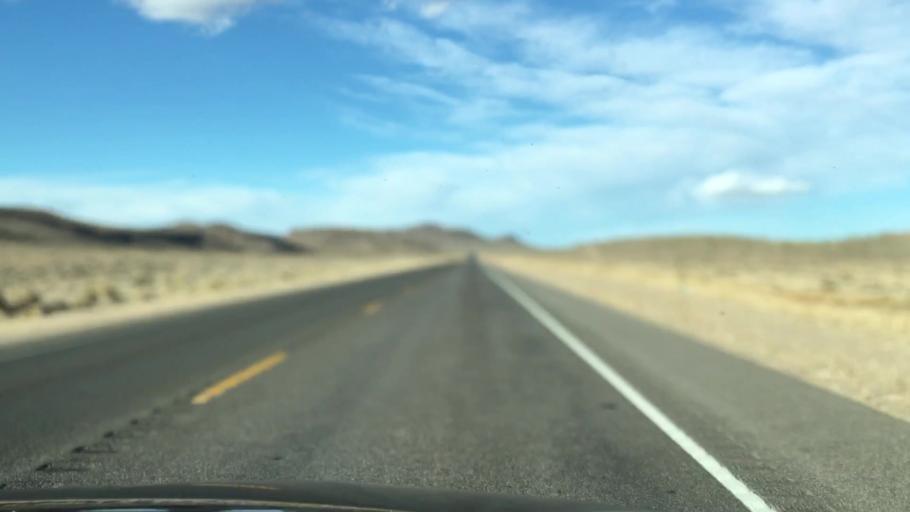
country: US
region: Nevada
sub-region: Esmeralda County
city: Goldfield
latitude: 37.6324
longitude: -117.2181
